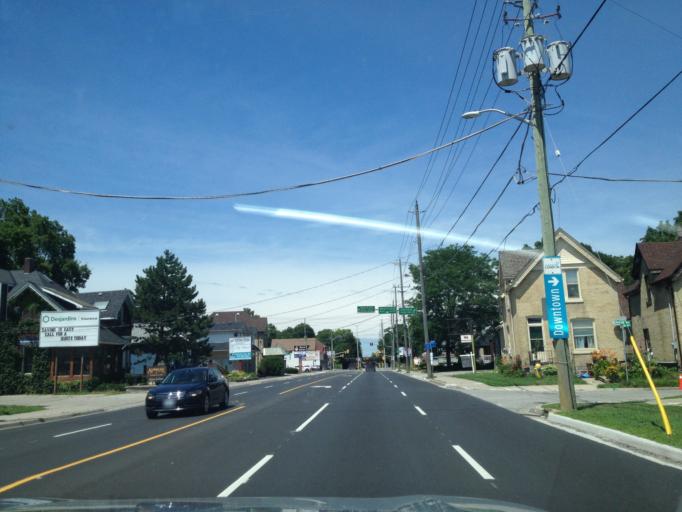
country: CA
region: Ontario
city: London
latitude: 42.9745
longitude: -81.2621
